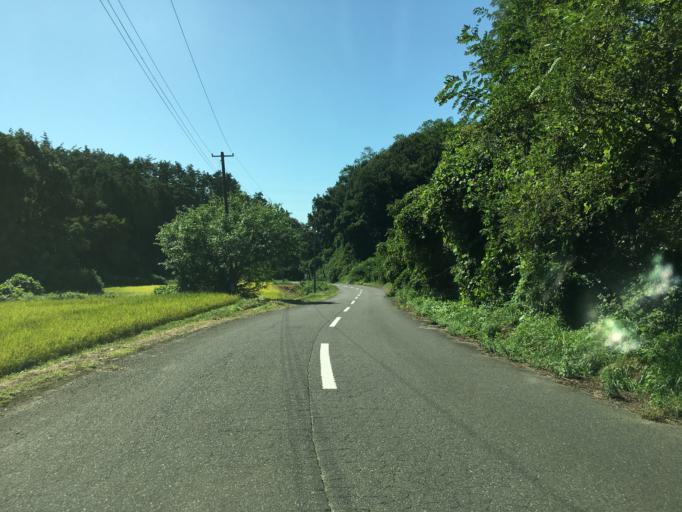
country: JP
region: Fukushima
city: Sukagawa
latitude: 37.2796
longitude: 140.4714
